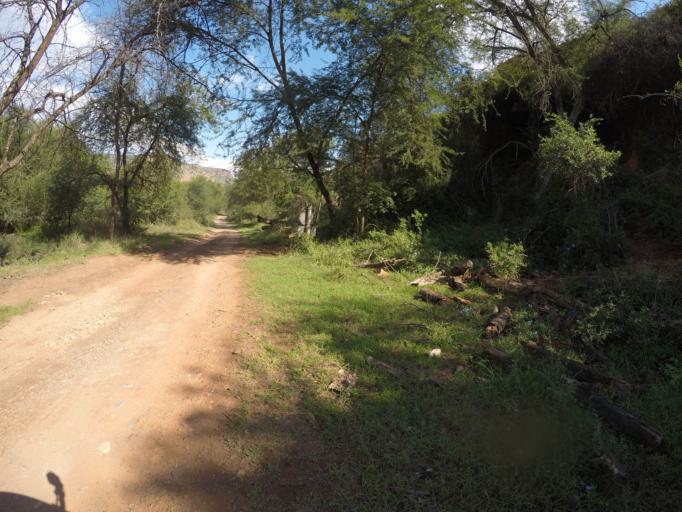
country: ZA
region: Eastern Cape
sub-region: Cacadu District Municipality
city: Kareedouw
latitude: -33.6637
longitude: 24.3894
